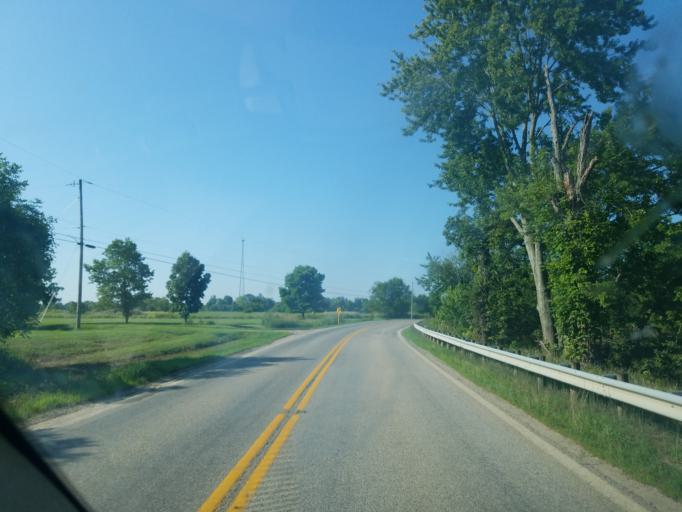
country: US
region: Ohio
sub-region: Marion County
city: Prospect
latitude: 40.4730
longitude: -83.1889
